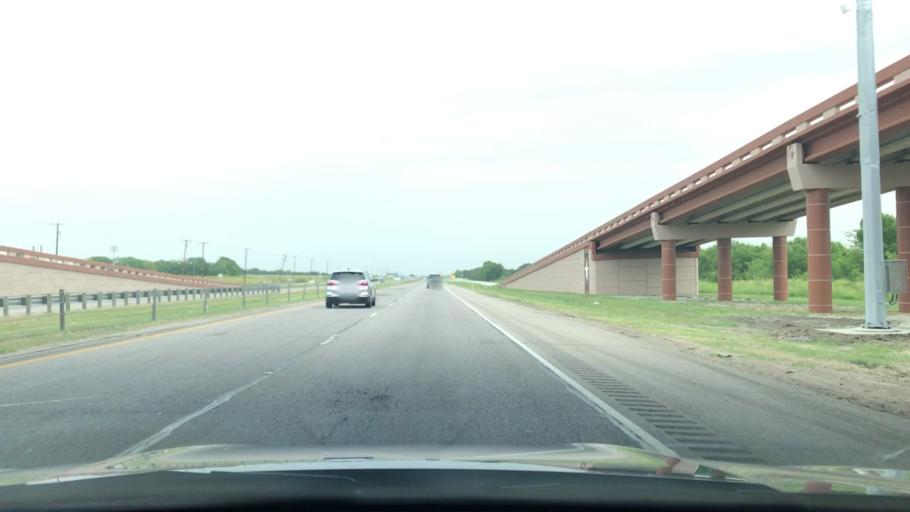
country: US
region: Texas
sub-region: Kaufman County
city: Forney
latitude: 32.7404
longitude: -96.4132
